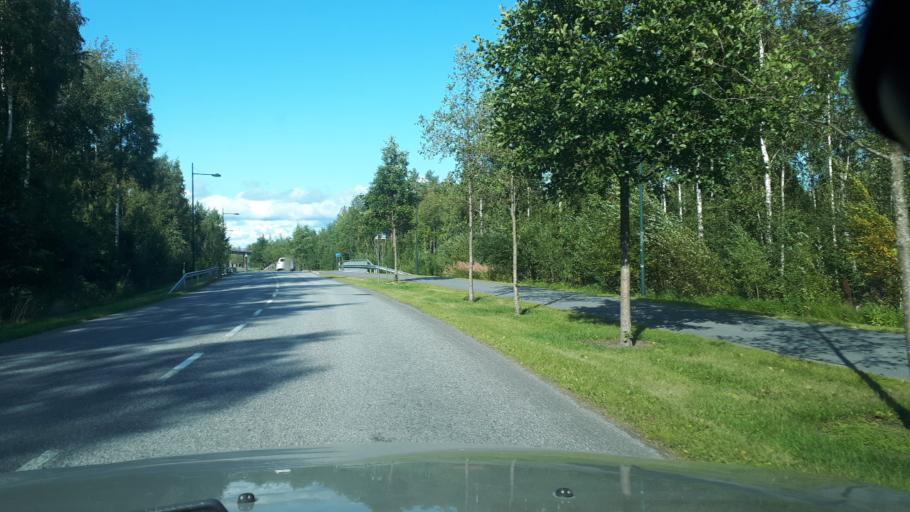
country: FI
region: Northern Ostrobothnia
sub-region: Oulu
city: Oulu
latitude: 65.0667
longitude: 25.4463
